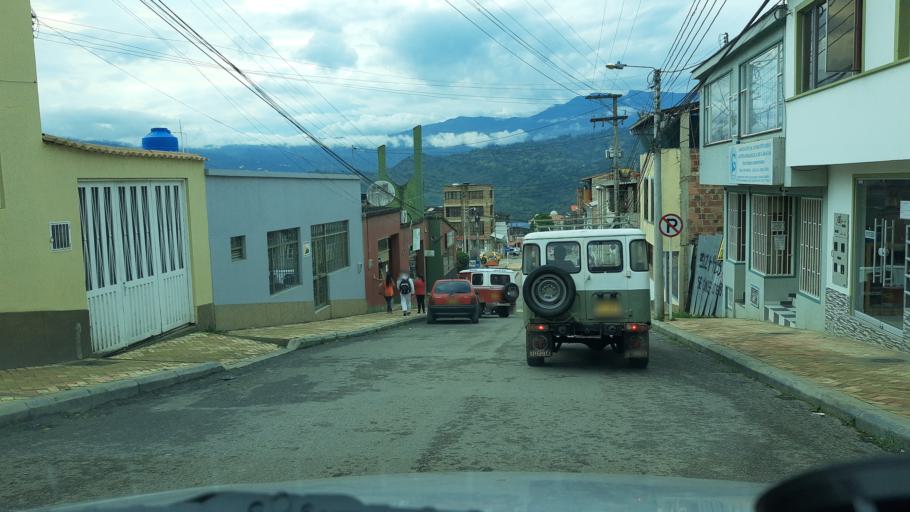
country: CO
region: Boyaca
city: Garagoa
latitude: 5.0843
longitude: -73.3644
